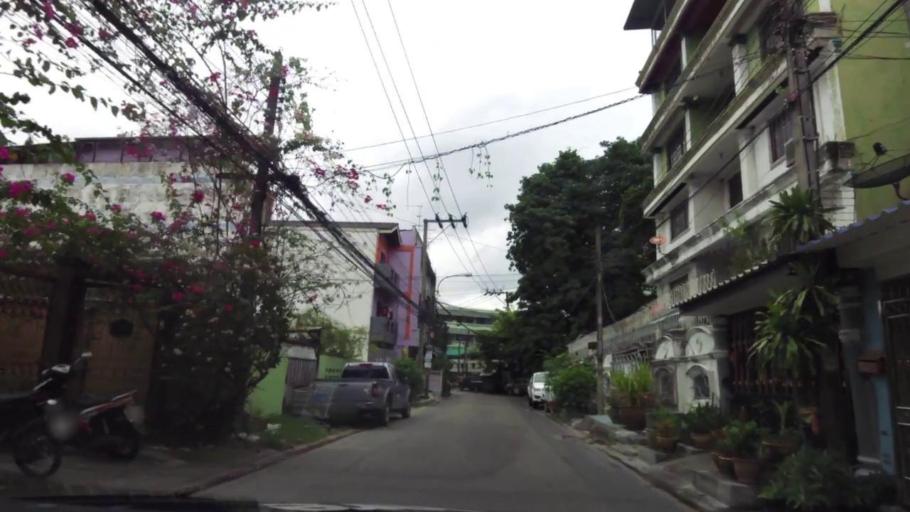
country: TH
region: Bangkok
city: Bang Kapi
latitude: 13.7715
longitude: 100.6459
